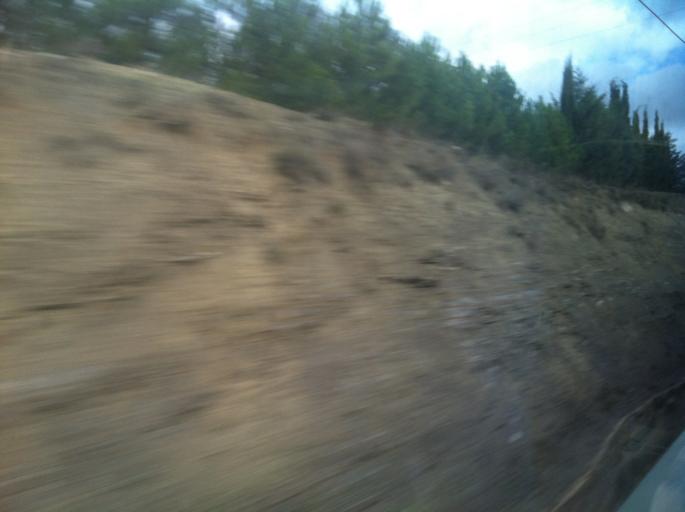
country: ES
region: Basque Country
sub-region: Provincia de Alava
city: Gasteiz / Vitoria
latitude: 42.8197
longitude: -2.7897
